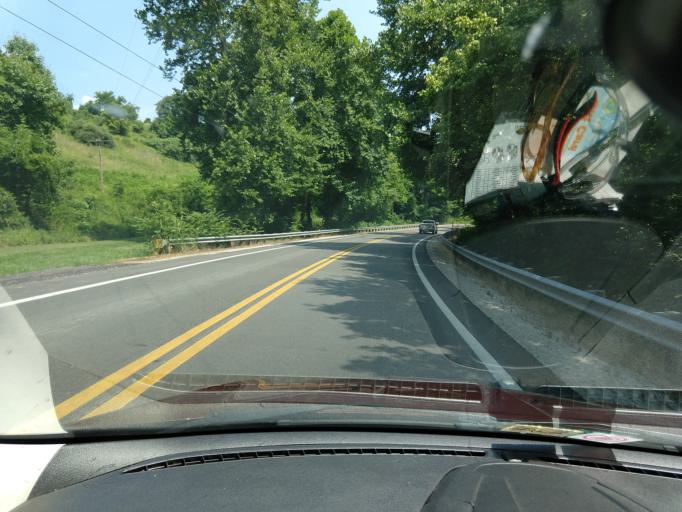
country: US
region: West Virginia
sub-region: Jackson County
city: Ravenswood
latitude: 38.8737
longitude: -81.8767
